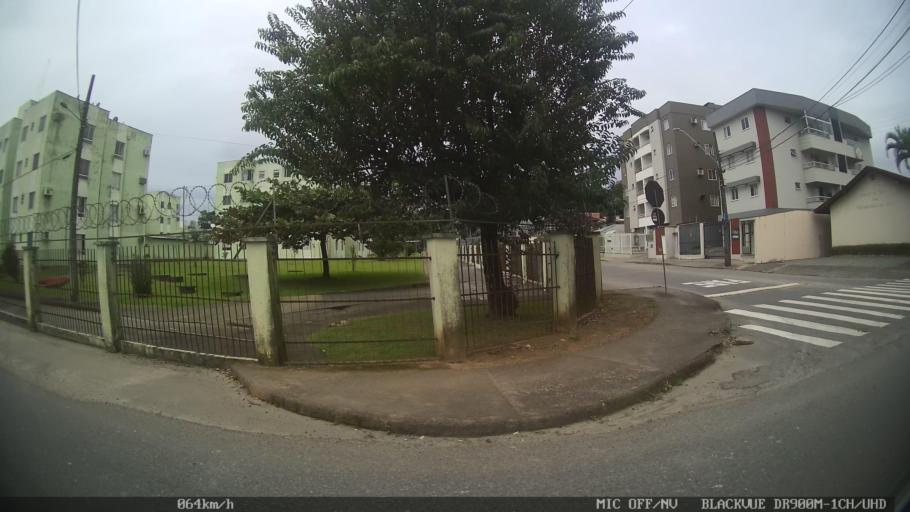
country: BR
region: Santa Catarina
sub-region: Joinville
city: Joinville
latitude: -26.2792
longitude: -48.8745
